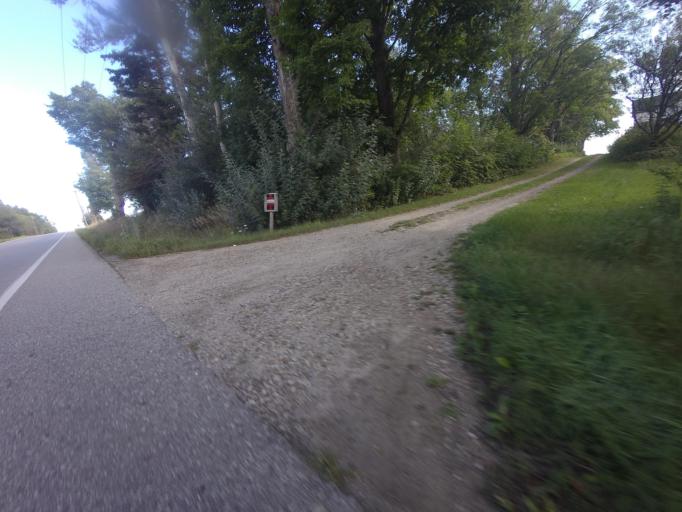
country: CA
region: Ontario
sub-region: Wellington County
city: Guelph
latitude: 43.5867
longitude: -80.3450
